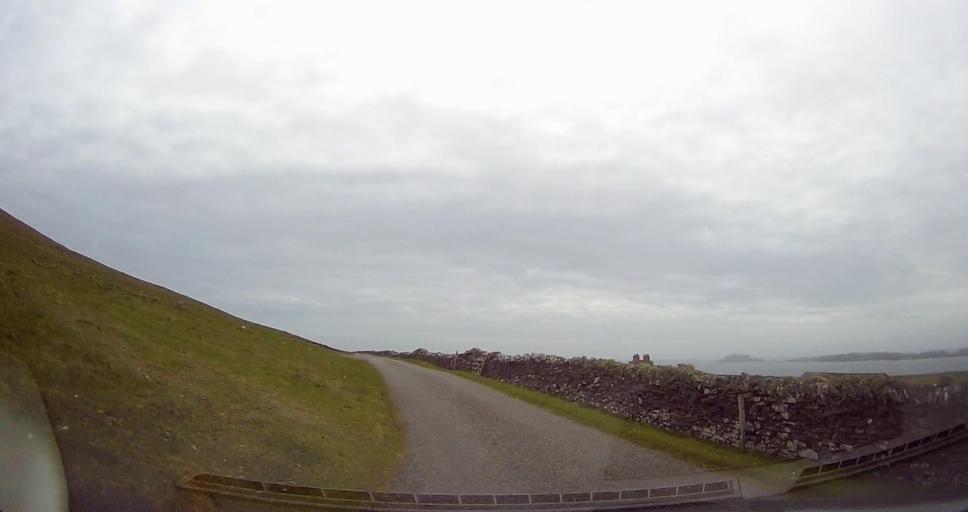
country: GB
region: Scotland
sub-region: Shetland Islands
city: Sandwick
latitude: 59.8698
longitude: -1.2787
